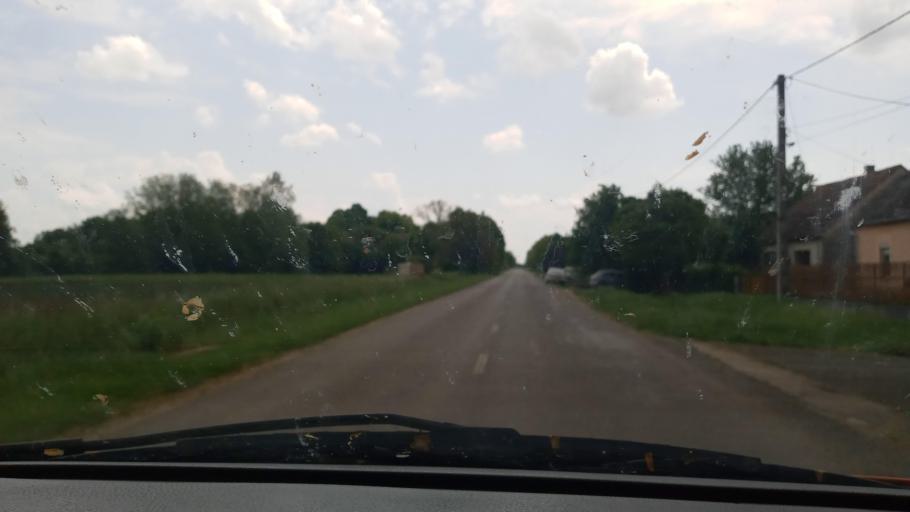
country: HU
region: Baranya
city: Beremend
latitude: 45.7777
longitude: 18.4411
